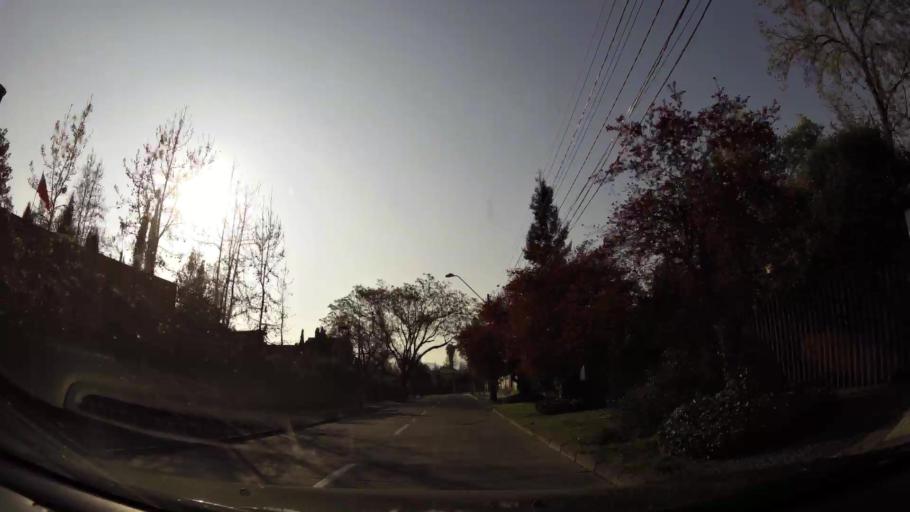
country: CL
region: Santiago Metropolitan
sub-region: Provincia de Santiago
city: Villa Presidente Frei, Nunoa, Santiago, Chile
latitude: -33.3568
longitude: -70.5302
